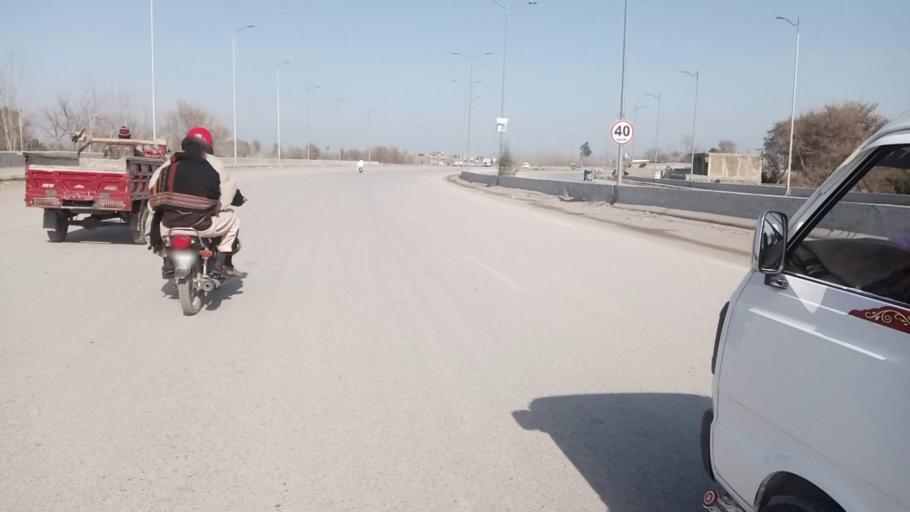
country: PK
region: Khyber Pakhtunkhwa
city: Peshawar
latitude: 34.0385
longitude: 71.5339
